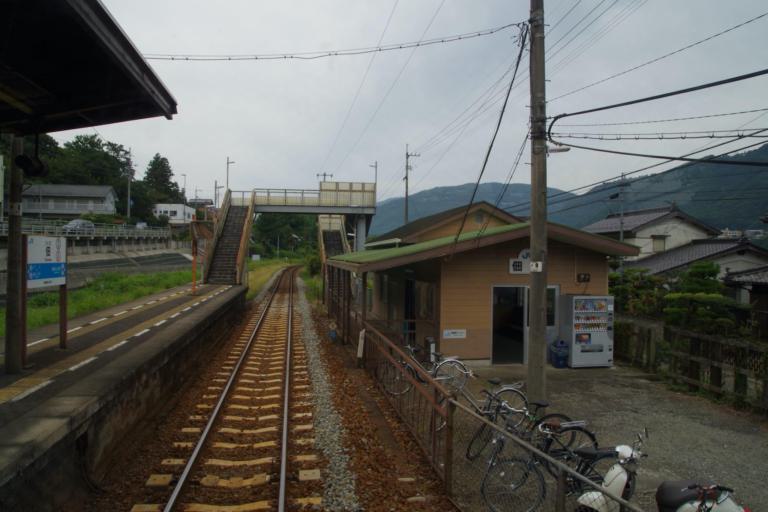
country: JP
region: Tokushima
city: Ikedacho
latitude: 34.0325
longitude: 133.8574
